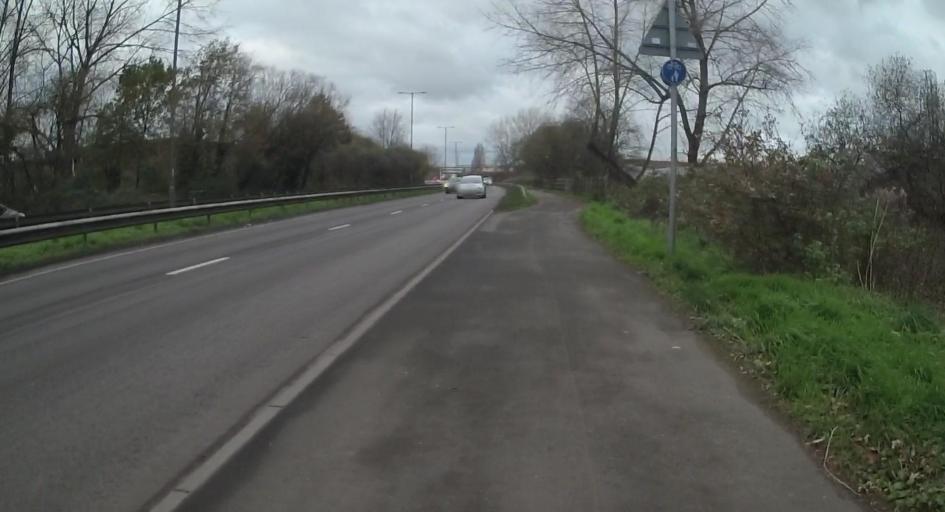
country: GB
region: England
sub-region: Surrey
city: Frimley
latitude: 51.3279
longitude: -0.7681
